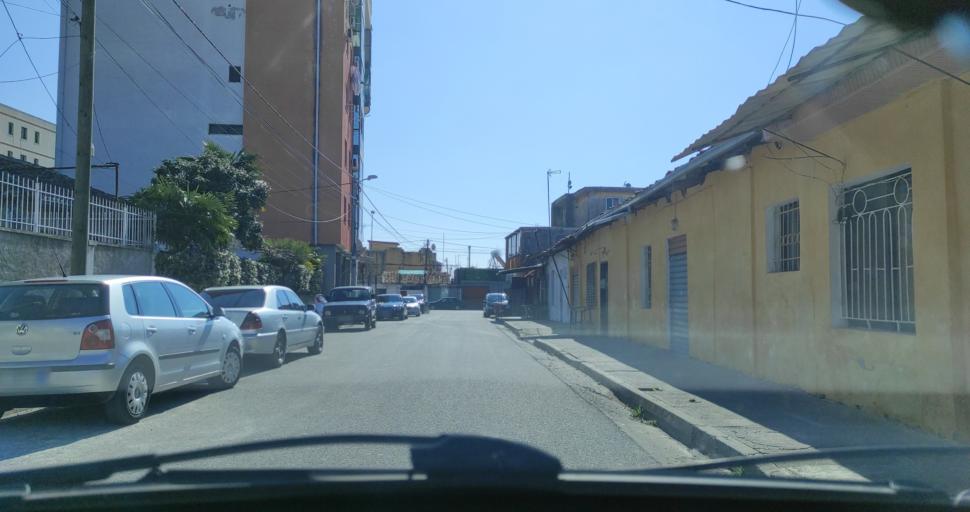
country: AL
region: Shkoder
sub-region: Rrethi i Shkodres
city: Shkoder
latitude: 42.0686
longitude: 19.5222
